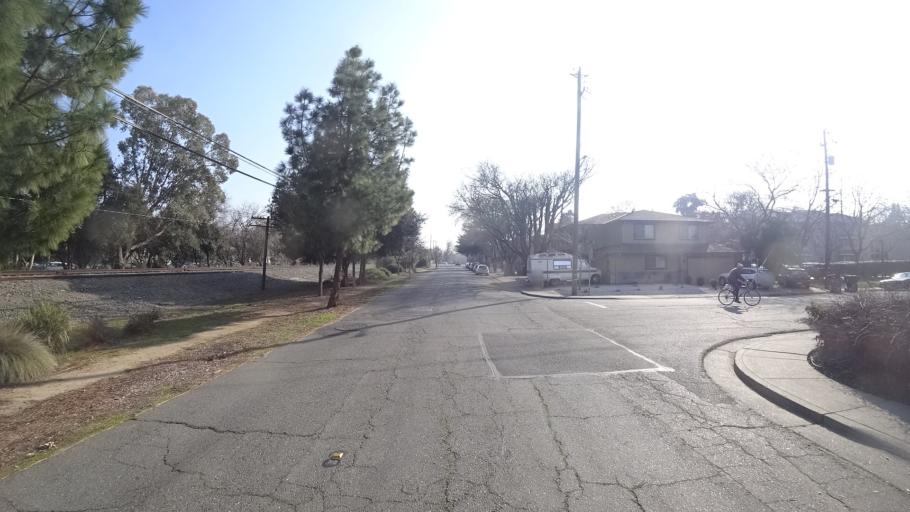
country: US
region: California
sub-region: Yolo County
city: Davis
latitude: 38.5531
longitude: -121.7409
